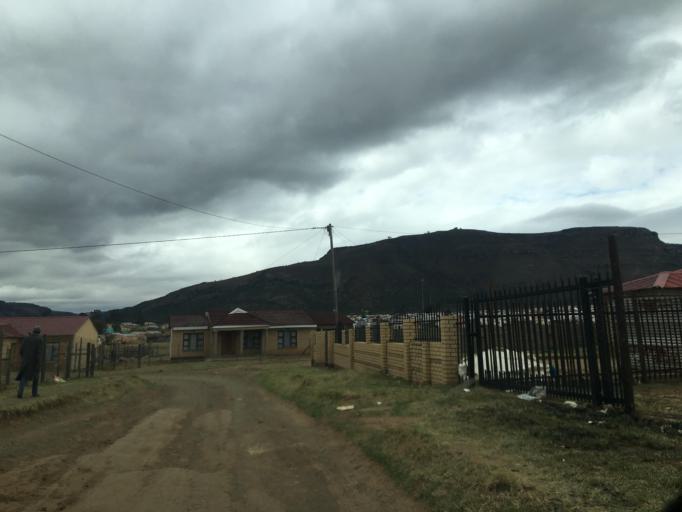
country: ZA
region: Eastern Cape
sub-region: Chris Hani District Municipality
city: Cala
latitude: -31.5365
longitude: 27.6966
